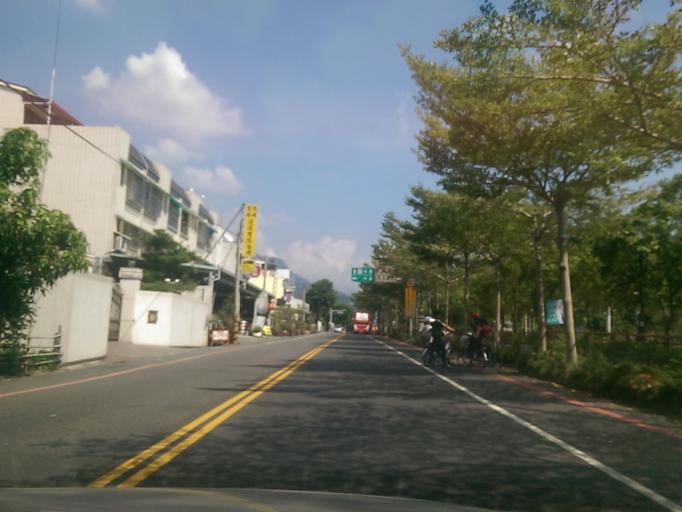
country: TW
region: Taiwan
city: Lugu
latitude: 23.8266
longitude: 120.7910
